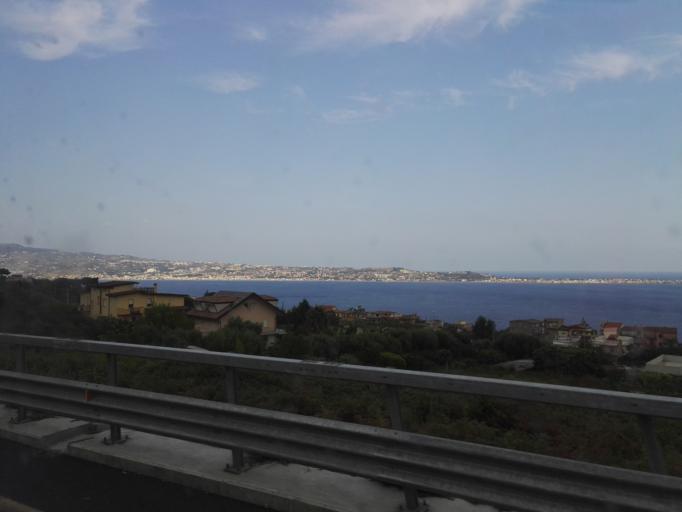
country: IT
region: Calabria
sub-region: Provincia di Reggio Calabria
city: Villa San Giovanni
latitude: 38.2285
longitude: 15.6506
